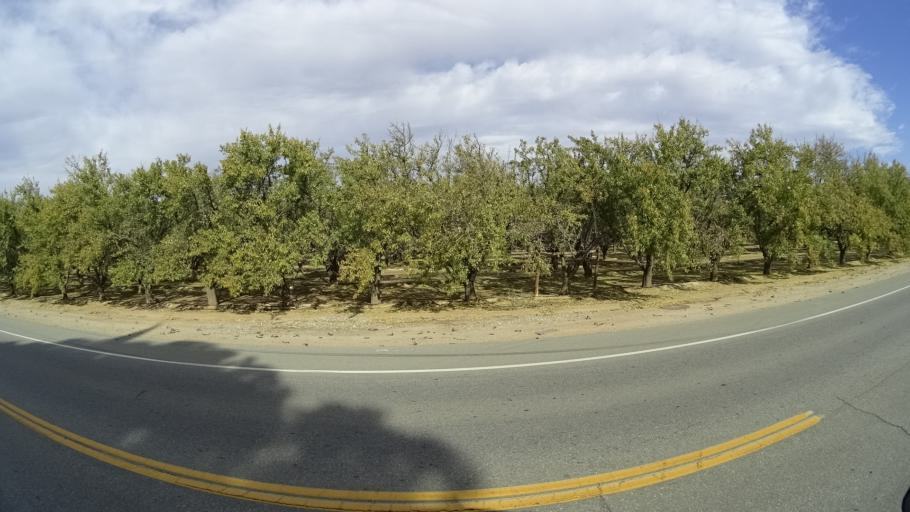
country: US
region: California
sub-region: Kern County
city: Greenacres
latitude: 35.4269
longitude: -119.0815
